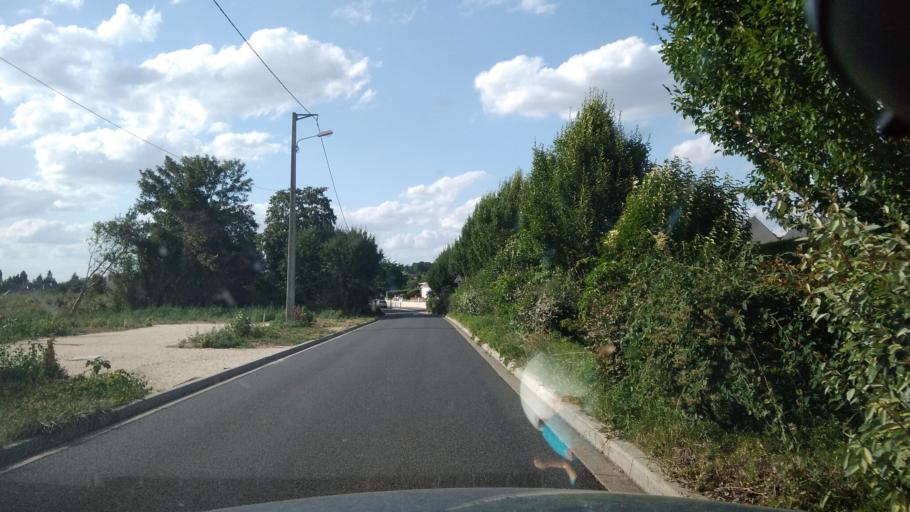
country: FR
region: Centre
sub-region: Departement d'Indre-et-Loire
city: Chambray-les-Tours
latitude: 47.3424
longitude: 0.6880
